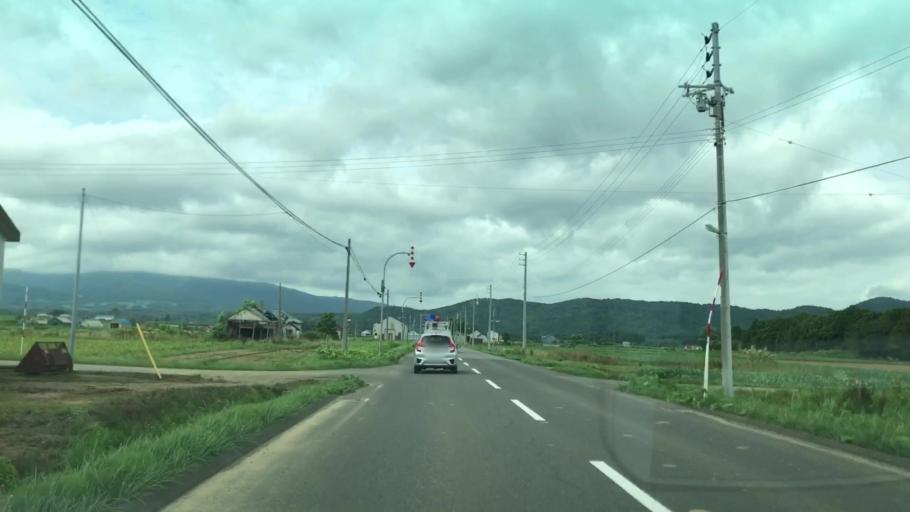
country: JP
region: Hokkaido
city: Niseko Town
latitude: 42.9327
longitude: 140.7831
